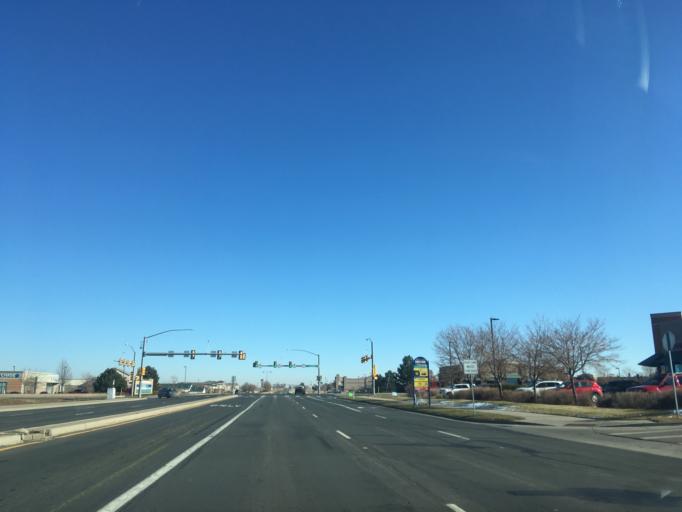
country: US
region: Colorado
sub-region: Weld County
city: Firestone
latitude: 40.1606
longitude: -104.9431
